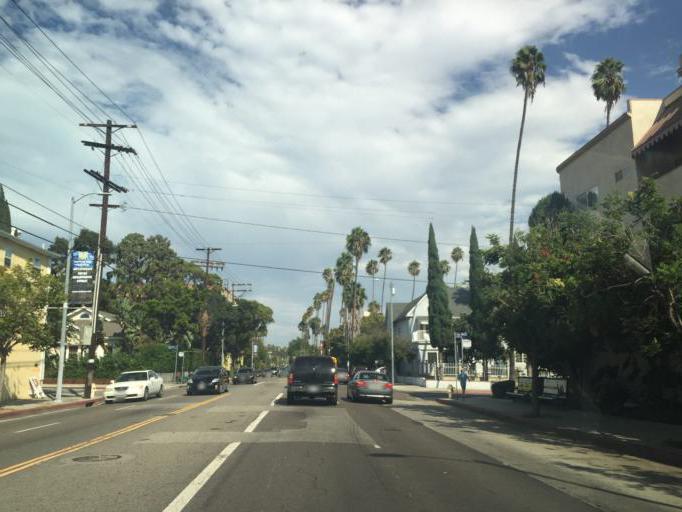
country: US
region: California
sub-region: Los Angeles County
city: Hollywood
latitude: 34.1053
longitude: -118.3163
